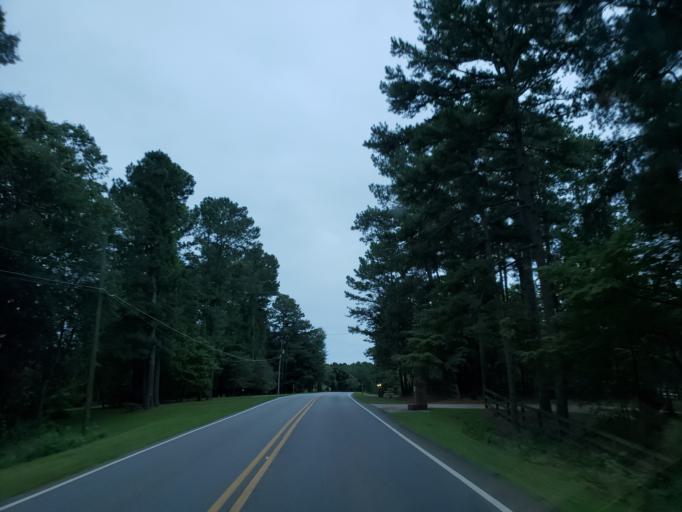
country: US
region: Georgia
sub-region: Cherokee County
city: Canton
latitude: 34.2846
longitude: -84.4523
